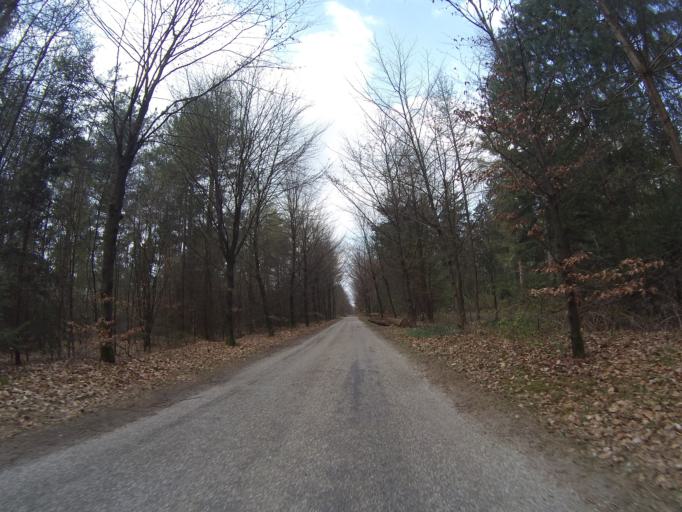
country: NL
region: North Holland
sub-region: Gemeente Hilversum
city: Hilversum
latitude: 52.1955
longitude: 5.2250
